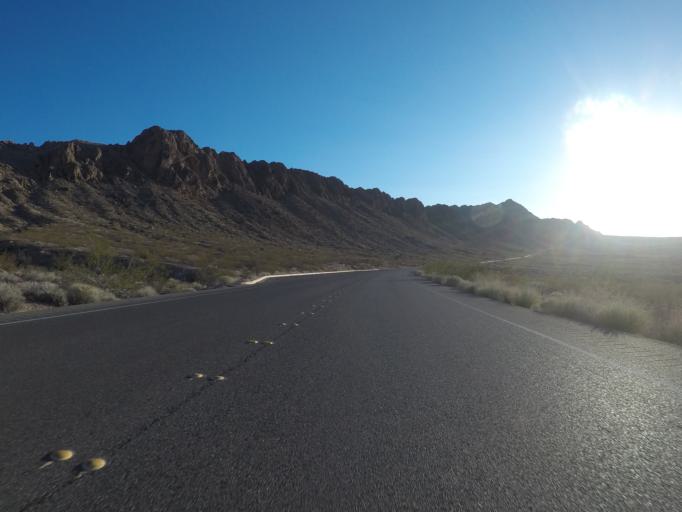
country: US
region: Nevada
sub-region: Clark County
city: Moapa Valley
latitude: 36.2538
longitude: -114.4824
